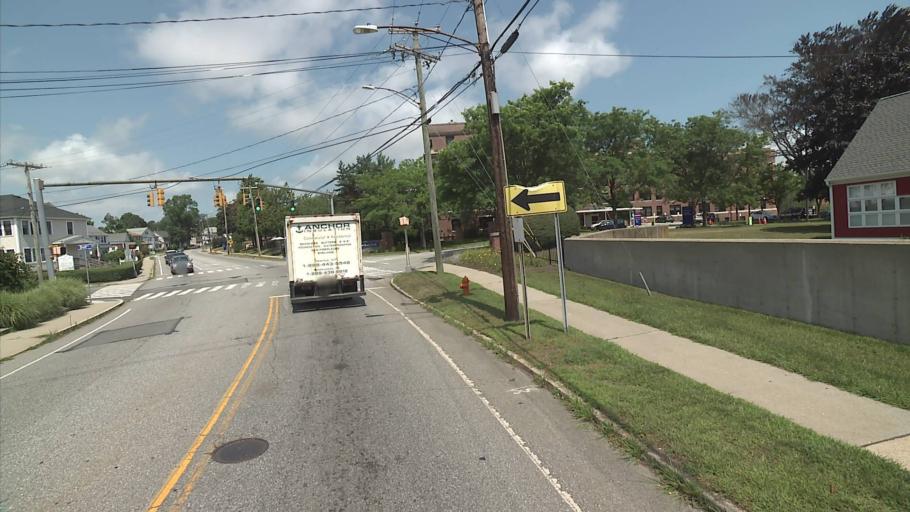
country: US
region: Connecticut
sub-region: New London County
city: New London
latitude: 41.3353
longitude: -72.1051
